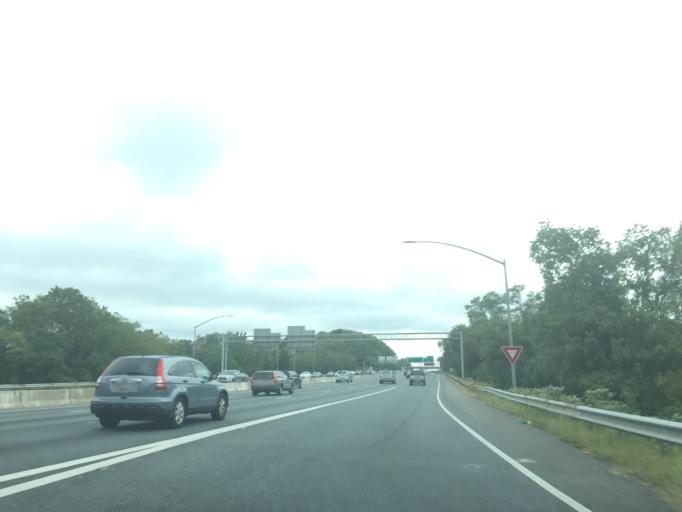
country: US
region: Maryland
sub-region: Baltimore County
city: Hampton
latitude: 39.4039
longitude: -76.5713
